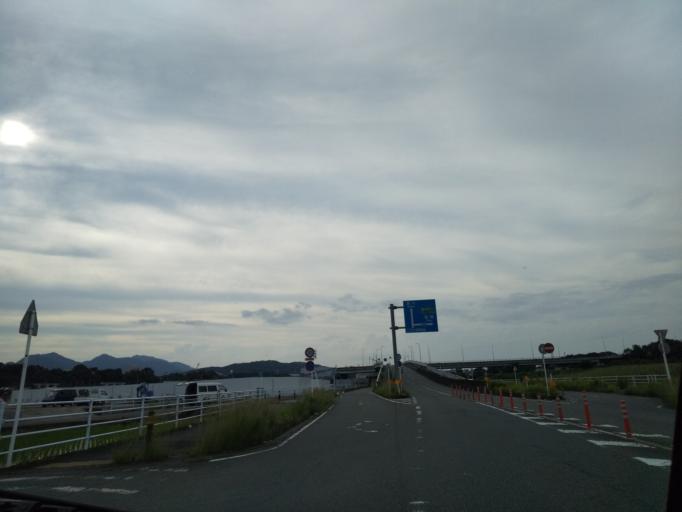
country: JP
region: Kanagawa
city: Zama
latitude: 35.4804
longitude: 139.3563
